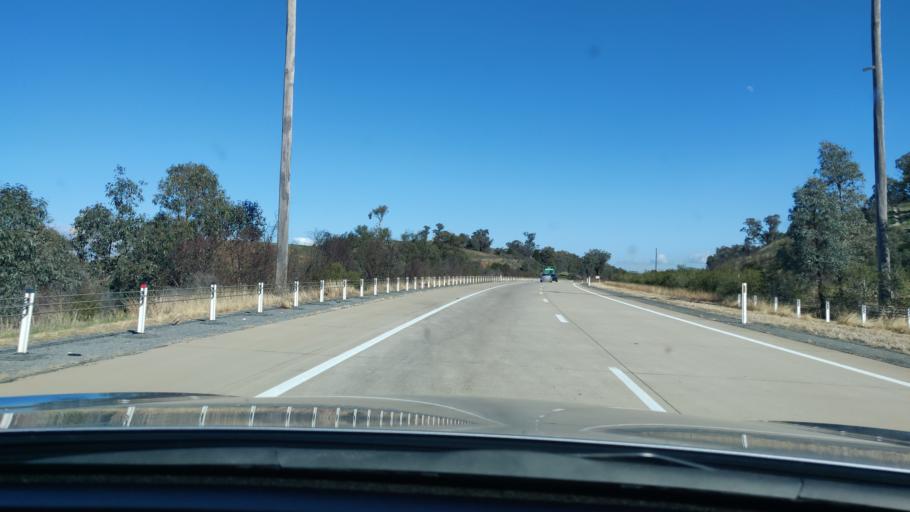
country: AU
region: New South Wales
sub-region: Wagga Wagga
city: Forest Hill
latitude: -35.2298
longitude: 147.7845
